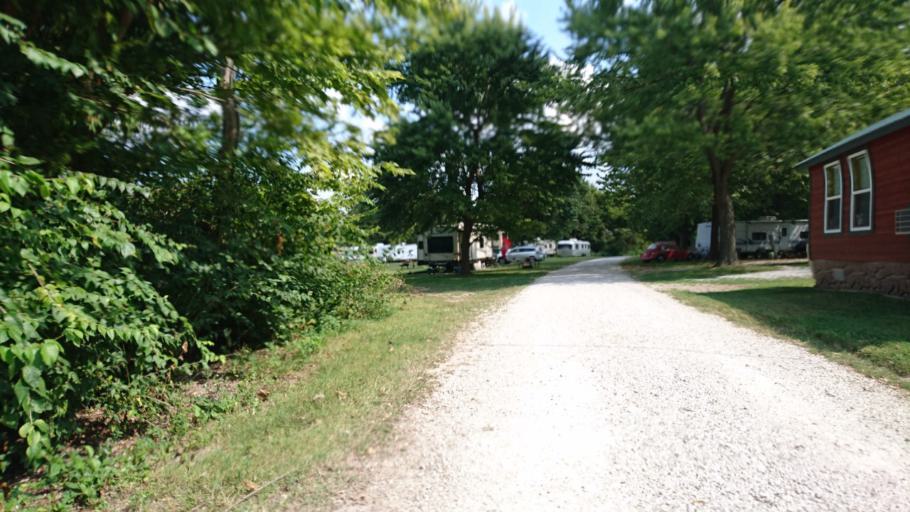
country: US
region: Missouri
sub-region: Greene County
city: Battlefield
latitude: 37.1998
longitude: -93.4027
